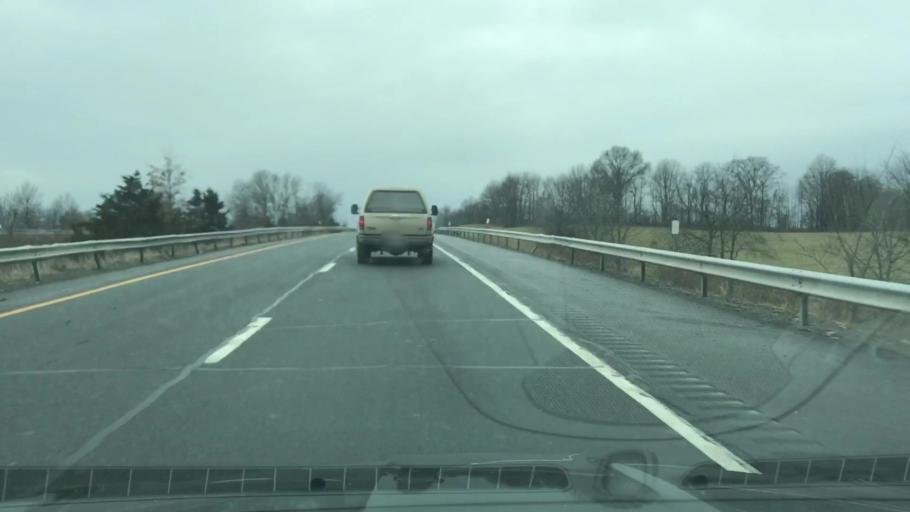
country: US
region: New York
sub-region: Orange County
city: Montgomery
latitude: 41.5008
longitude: -74.2393
